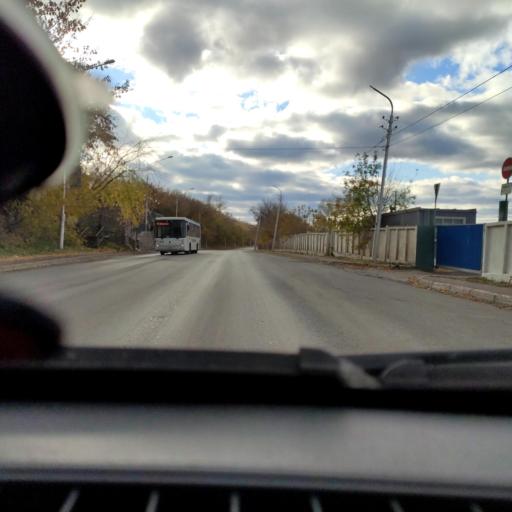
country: RU
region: Bashkortostan
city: Ufa
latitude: 54.7459
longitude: 55.9430
